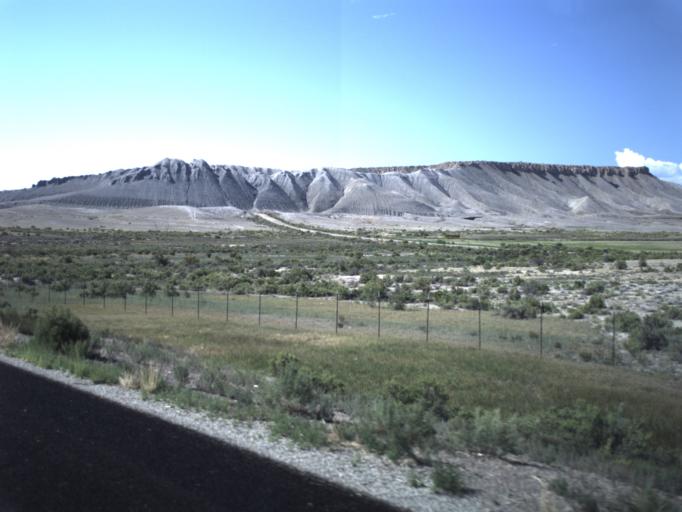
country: US
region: Utah
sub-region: Emery County
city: Ferron
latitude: 39.0618
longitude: -111.1304
